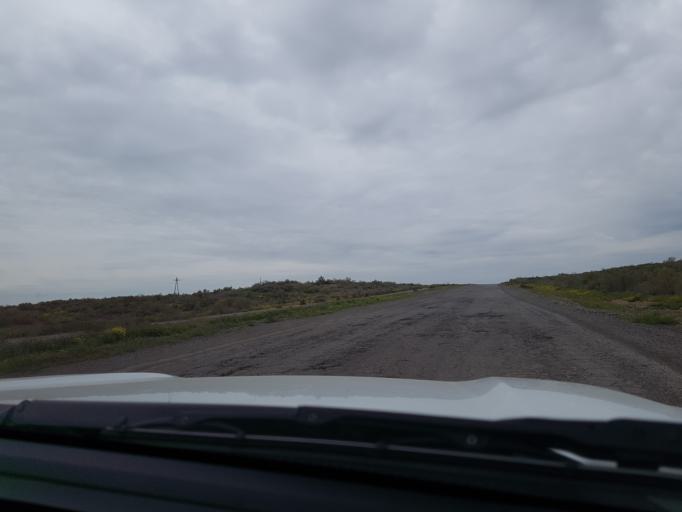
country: TM
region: Mary
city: Bayramaly
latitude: 37.9145
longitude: 62.6218
